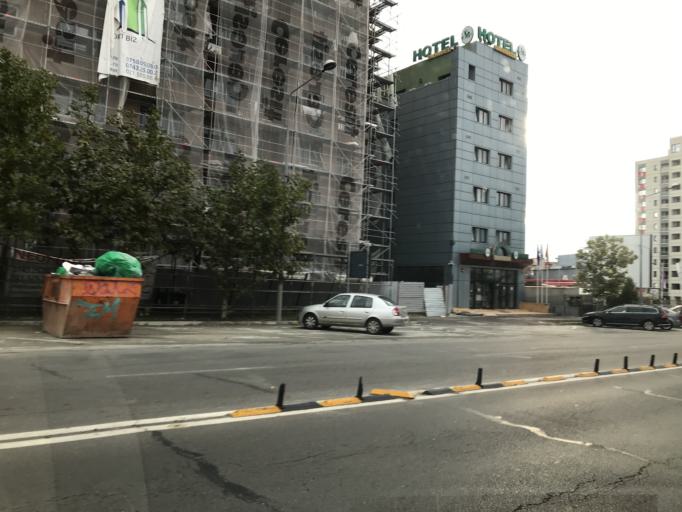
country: RO
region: Bucuresti
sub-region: Municipiul Bucuresti
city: Bucuresti
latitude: 44.4472
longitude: 26.0617
